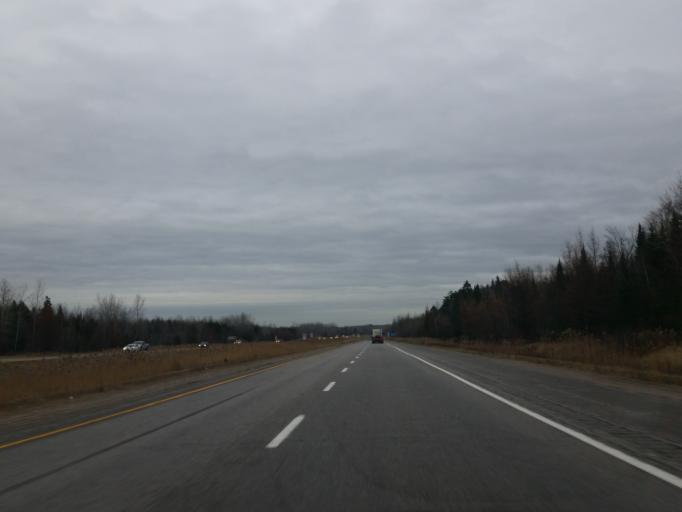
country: CA
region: Quebec
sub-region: Capitale-Nationale
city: Saint-Marc-des-Carrieres
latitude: 46.6021
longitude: -72.1335
